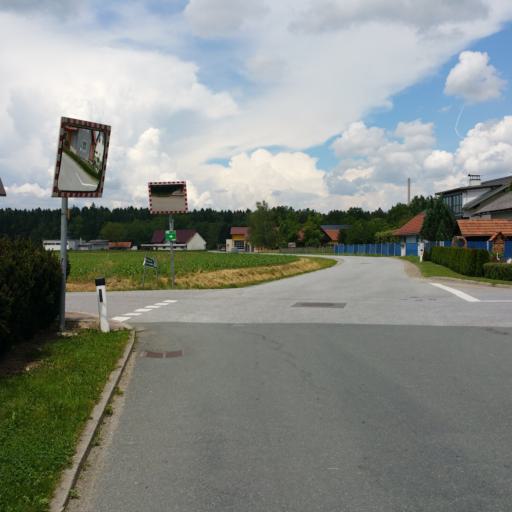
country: AT
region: Styria
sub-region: Politischer Bezirk Leibnitz
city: Gleinstatten
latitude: 46.7464
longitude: 15.3507
